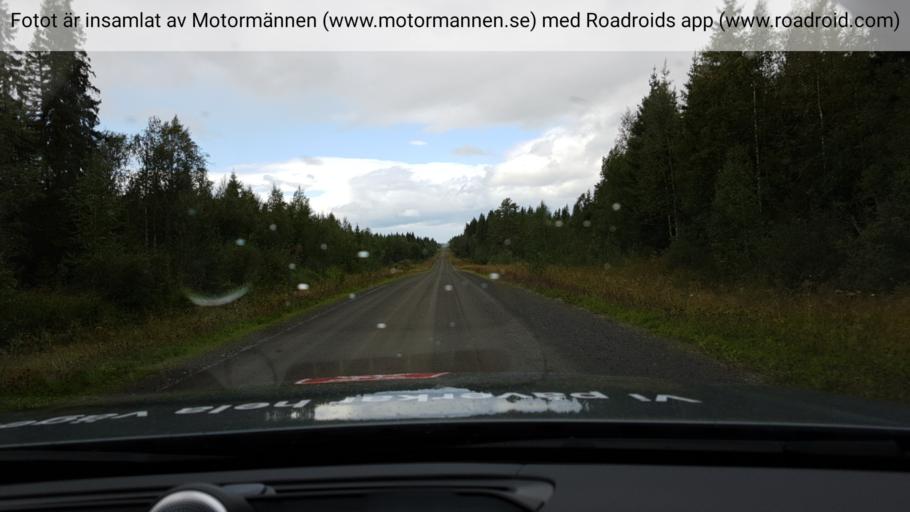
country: SE
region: Jaemtland
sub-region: OEstersunds Kommun
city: Lit
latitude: 63.6649
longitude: 14.9017
